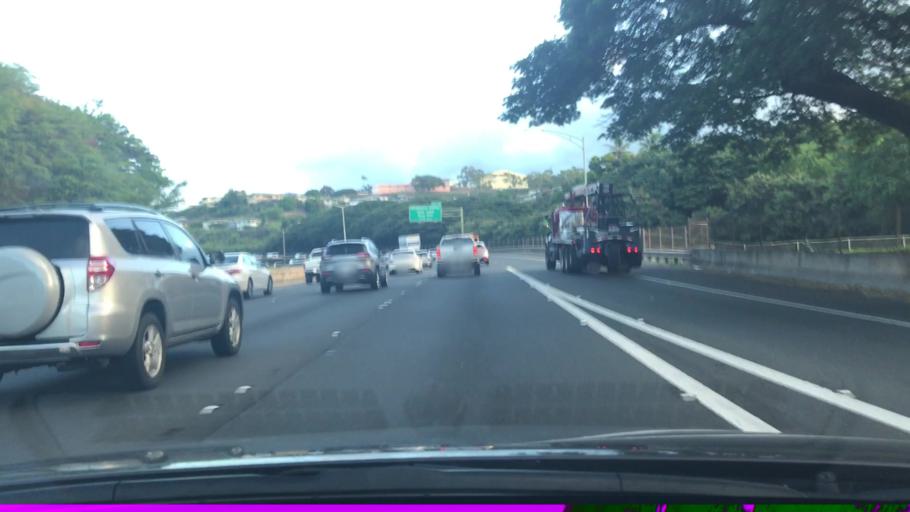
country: US
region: Hawaii
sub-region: Honolulu County
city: Halawa Heights
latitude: 21.3521
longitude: -157.8963
